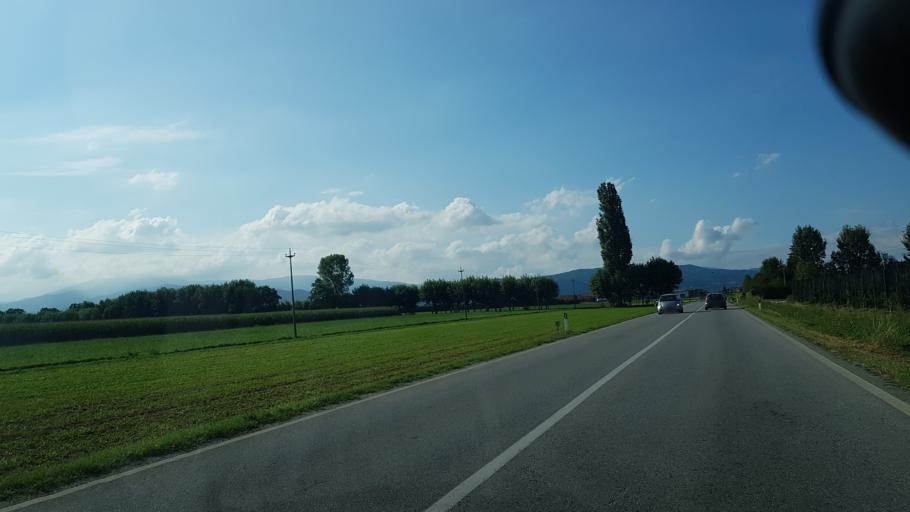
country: IT
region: Piedmont
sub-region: Provincia di Cuneo
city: Roata Rossi
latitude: 44.4663
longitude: 7.5147
